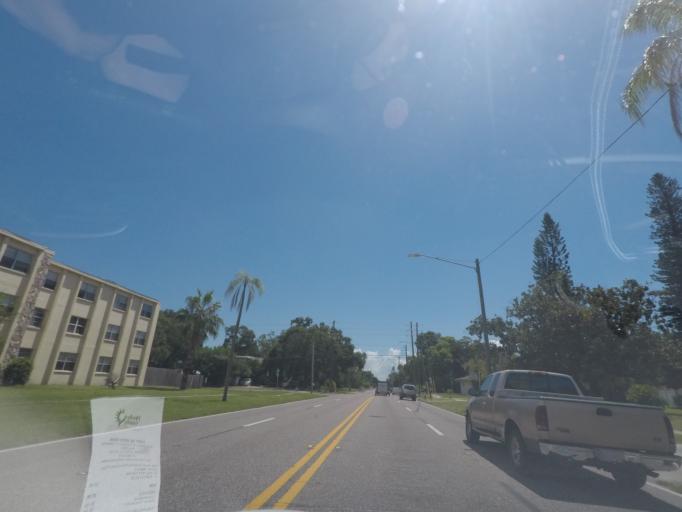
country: US
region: Florida
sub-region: Pinellas County
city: Gulfport
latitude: 27.7483
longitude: -82.6963
